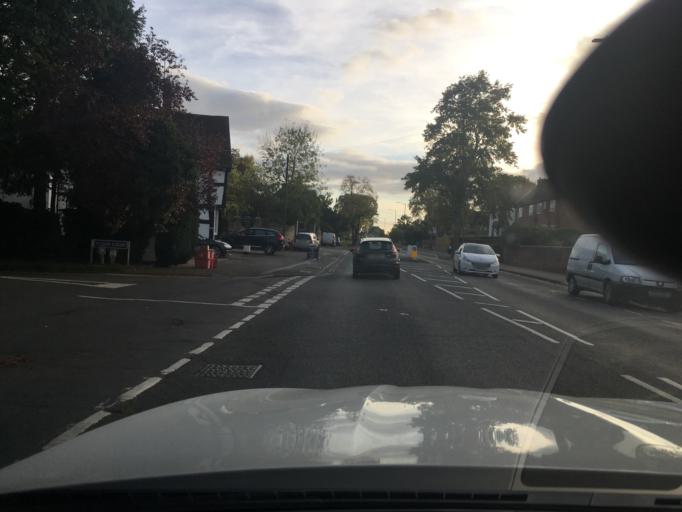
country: GB
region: England
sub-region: Warwickshire
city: Warwick
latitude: 52.2771
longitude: -1.5933
